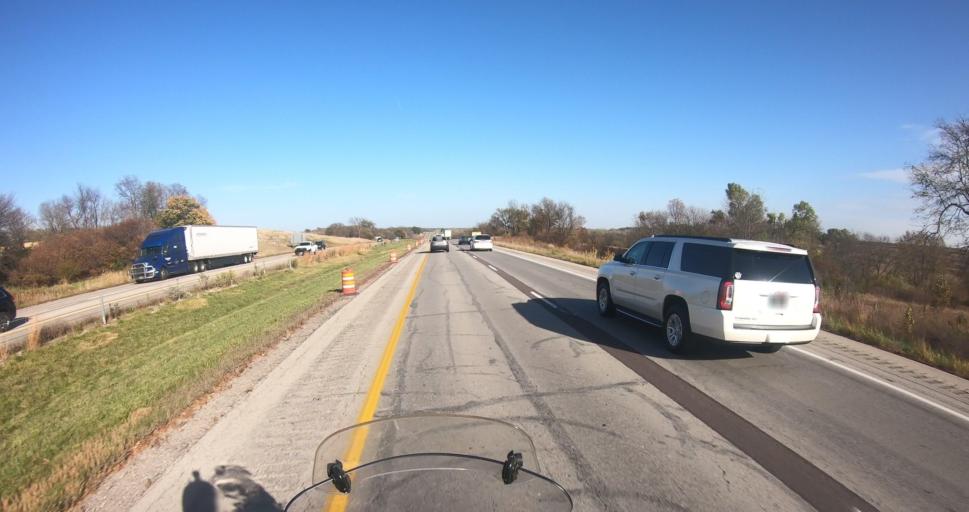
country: US
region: Iowa
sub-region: Dallas County
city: De Soto
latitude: 41.5421
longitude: -93.9942
